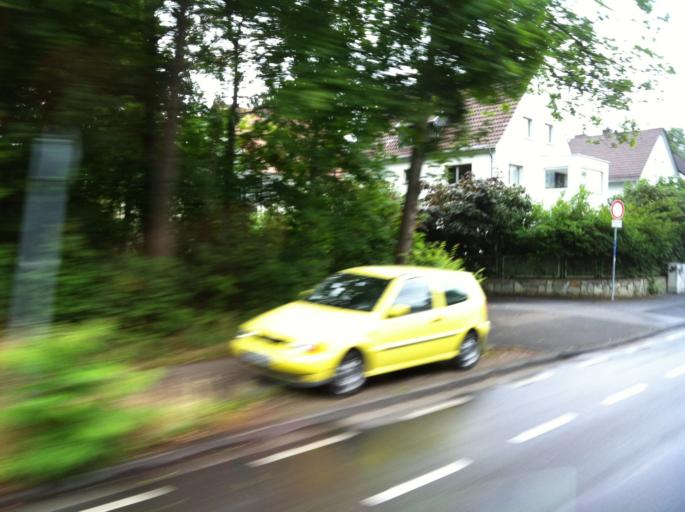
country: DE
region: Rheinland-Pfalz
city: Mainz
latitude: 50.0028
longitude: 8.2421
